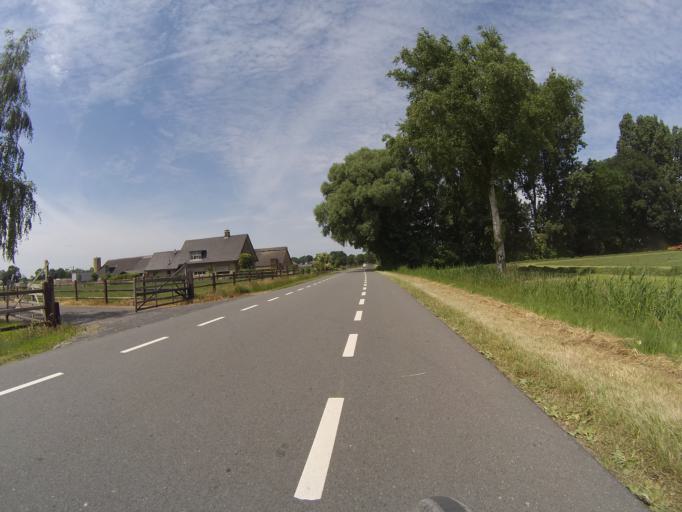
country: NL
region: Gelderland
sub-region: Gemeente Ede
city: Lunteren
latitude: 52.1118
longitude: 5.6287
